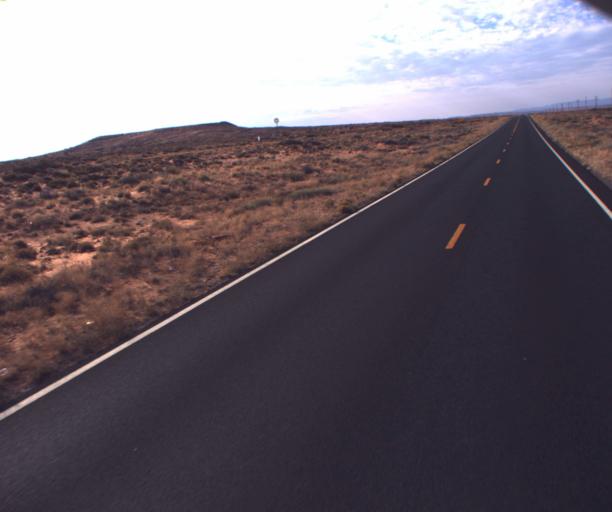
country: US
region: Arizona
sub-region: Apache County
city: Many Farms
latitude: 36.8733
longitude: -109.6316
